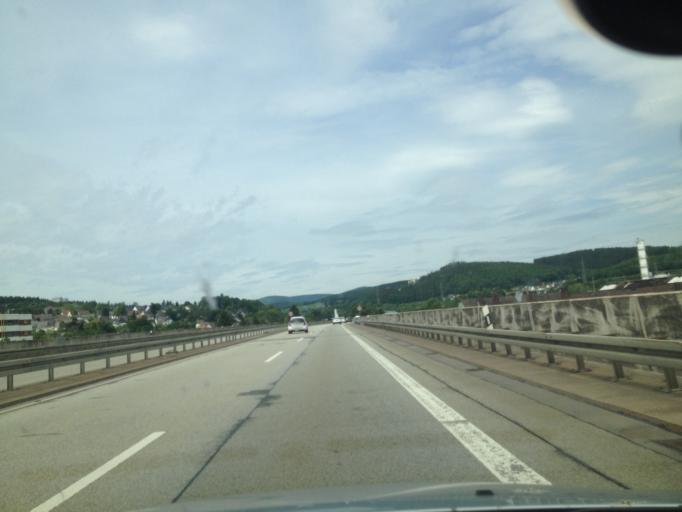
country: DE
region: North Rhine-Westphalia
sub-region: Regierungsbezirk Arnsberg
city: Siegen
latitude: 50.9151
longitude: 8.0132
